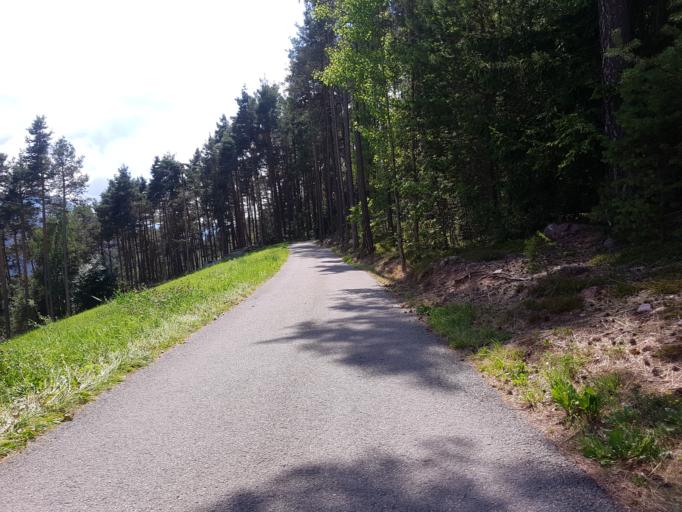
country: IT
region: Trentino-Alto Adige
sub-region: Bolzano
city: Siusi
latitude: 46.5505
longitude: 11.5491
